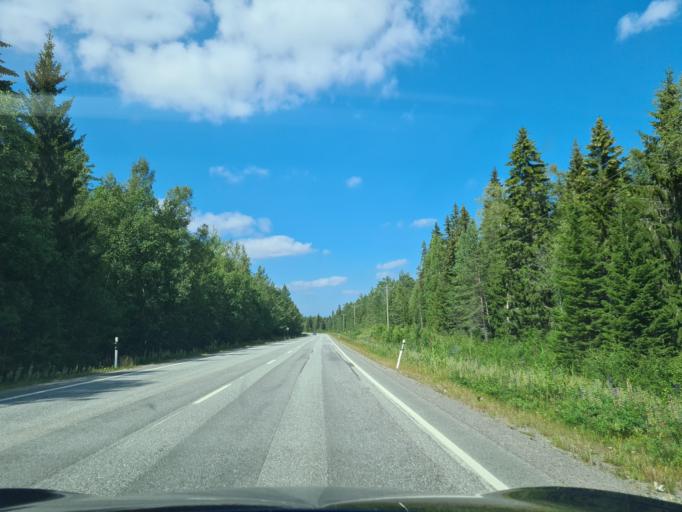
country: FI
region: Ostrobothnia
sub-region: Vaasa
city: Vaasa
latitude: 63.1750
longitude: 21.5780
